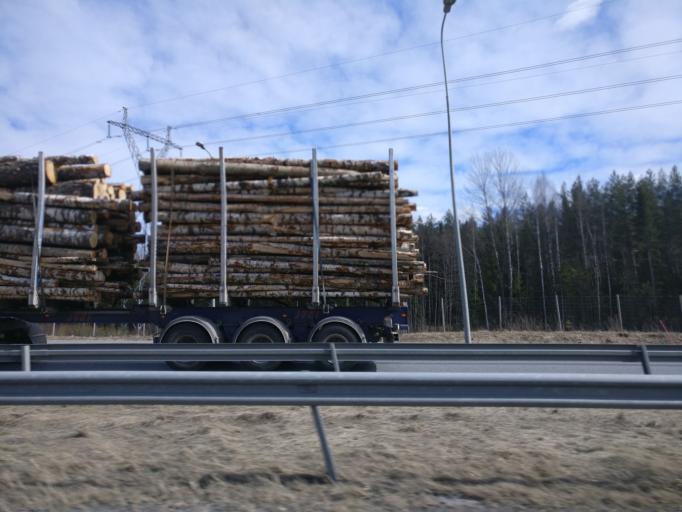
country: FI
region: Pirkanmaa
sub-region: Tampere
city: Tampere
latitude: 61.4475
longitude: 23.7651
